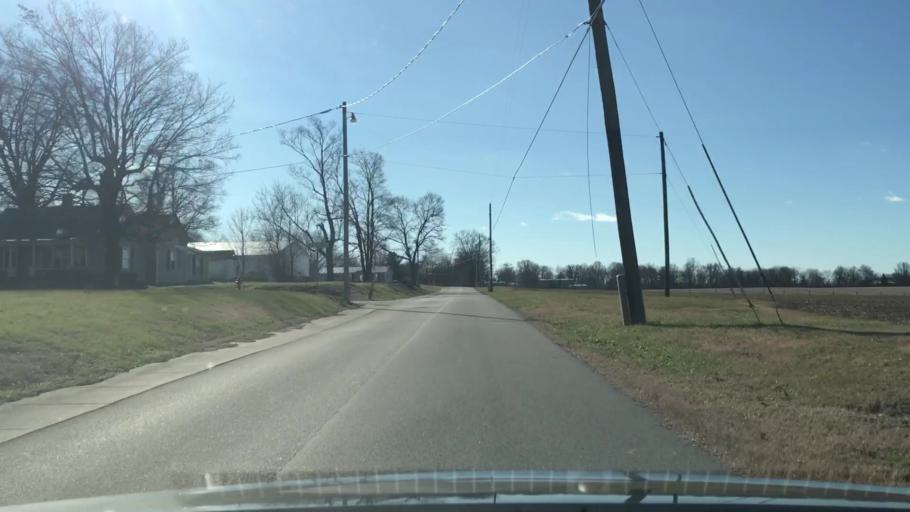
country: US
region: Kentucky
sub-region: Edmonson County
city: Brownsville
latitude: 37.0568
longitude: -86.2111
